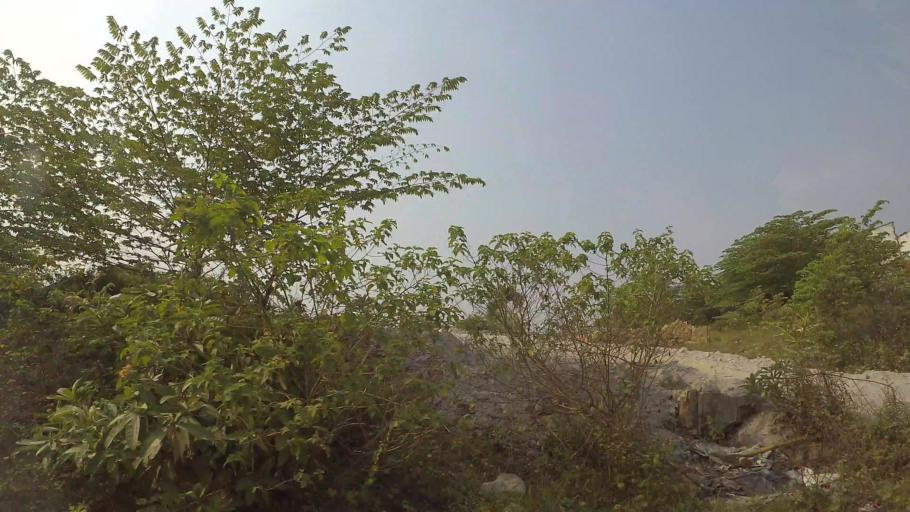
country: VN
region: Da Nang
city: Cam Le
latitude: 15.9972
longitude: 108.2175
